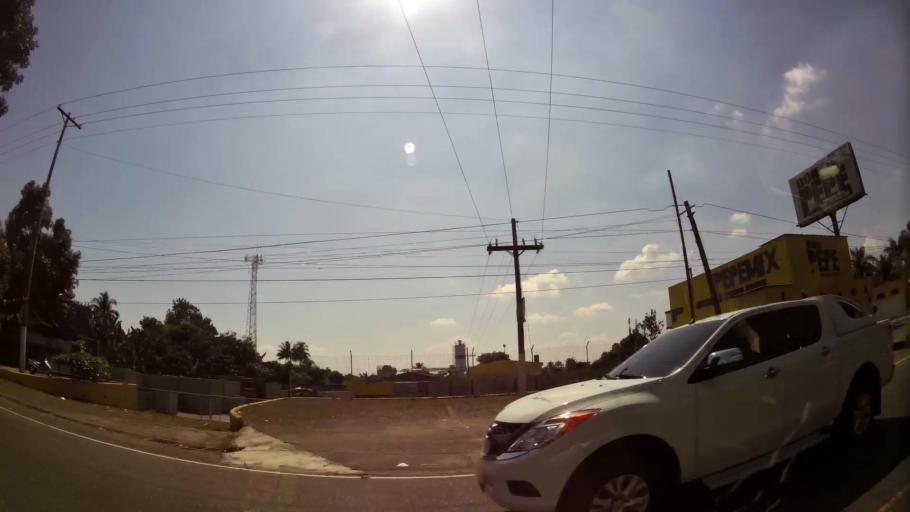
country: GT
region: Suchitepeque
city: Mazatenango
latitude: 14.5337
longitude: -91.4899
